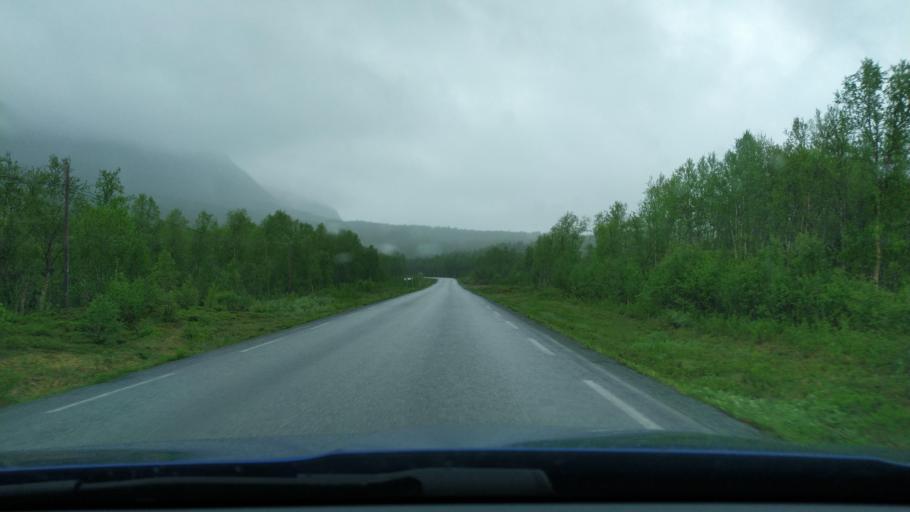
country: NO
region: Troms
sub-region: Dyroy
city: Brostadbotn
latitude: 69.0249
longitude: 17.7382
